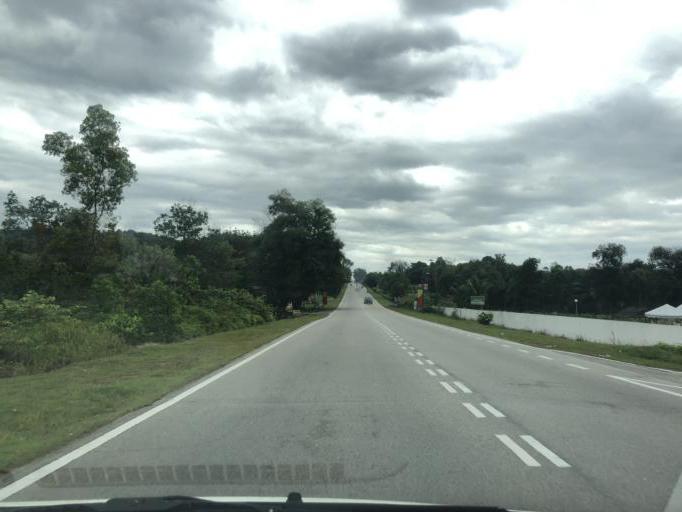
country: MY
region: Putrajaya
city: Putrajaya
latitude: 2.9260
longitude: 101.7472
